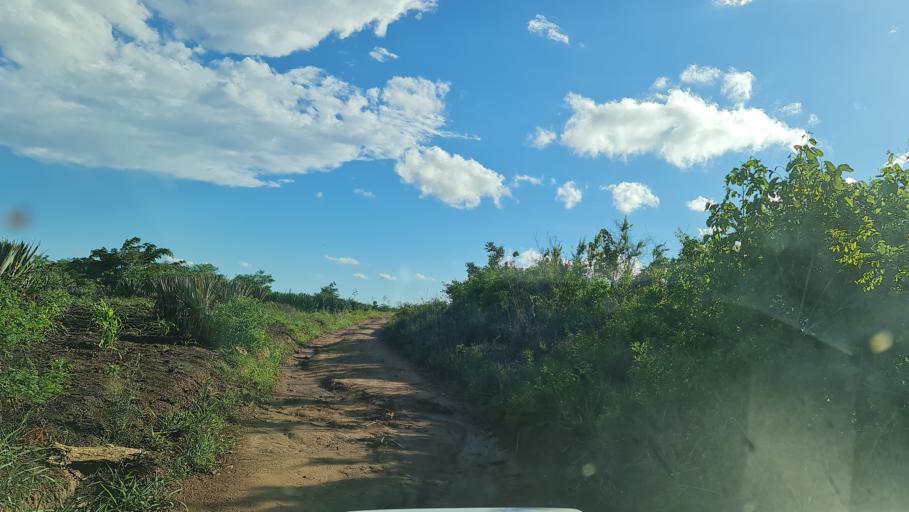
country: MZ
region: Nampula
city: Ilha de Mocambique
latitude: -14.9408
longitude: 40.1998
